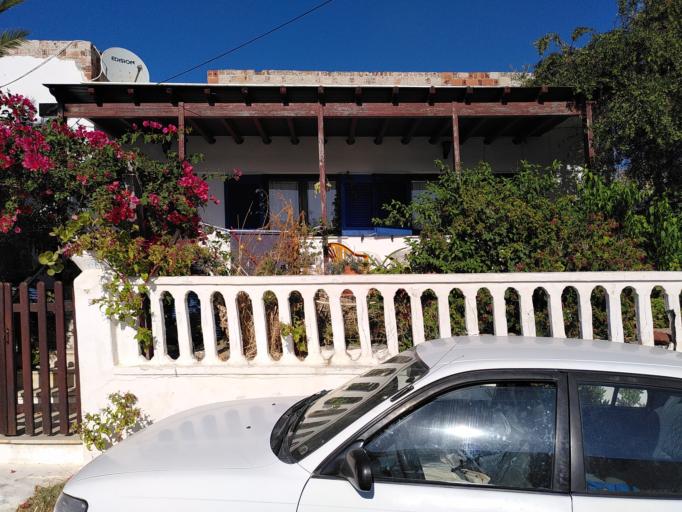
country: GR
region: South Aegean
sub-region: Nomos Kykladon
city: Amorgos
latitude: 36.9071
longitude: 25.9785
